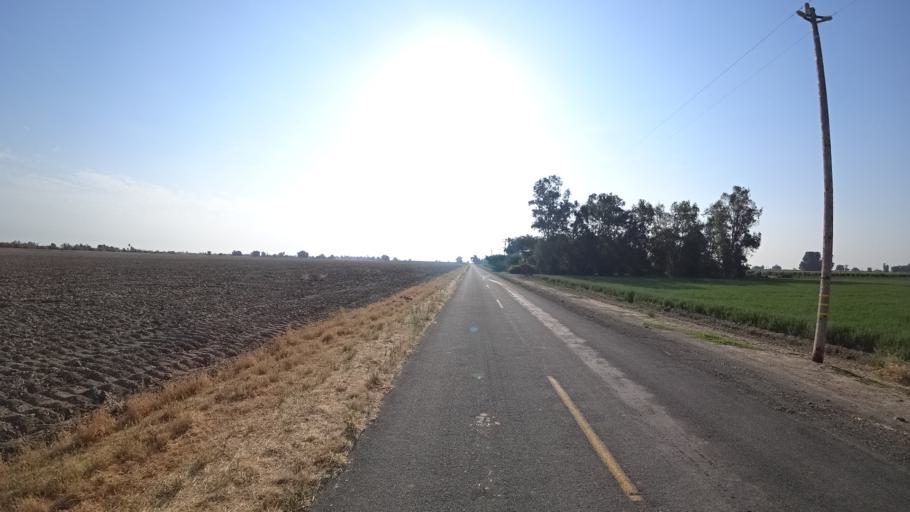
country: US
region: California
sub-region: Fresno County
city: Riverdale
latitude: 36.3805
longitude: -119.8066
